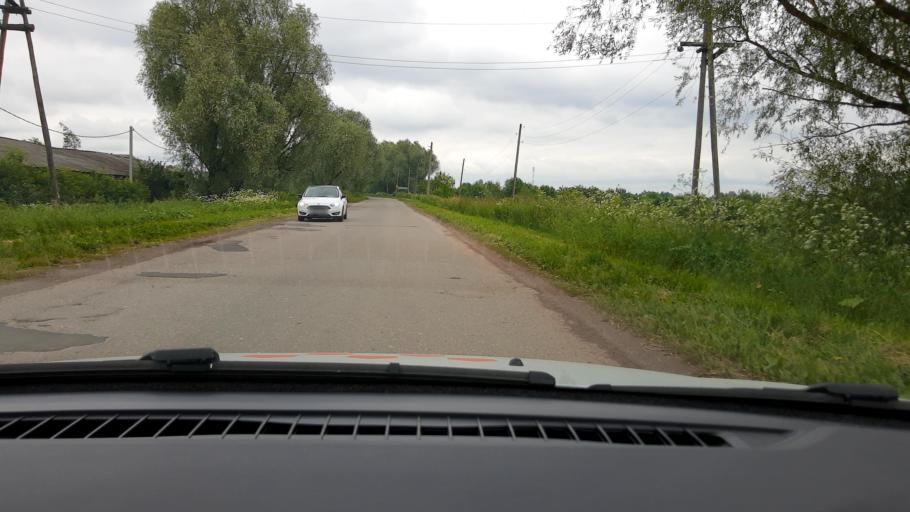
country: RU
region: Nizjnij Novgorod
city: Bogorodsk
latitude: 56.0733
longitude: 43.5080
